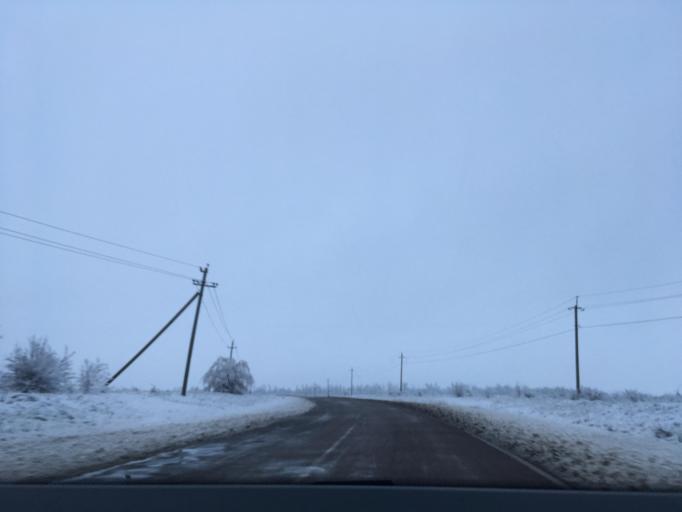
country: RU
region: Voronezj
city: Verkhniy Mamon
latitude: 50.0333
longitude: 40.0541
